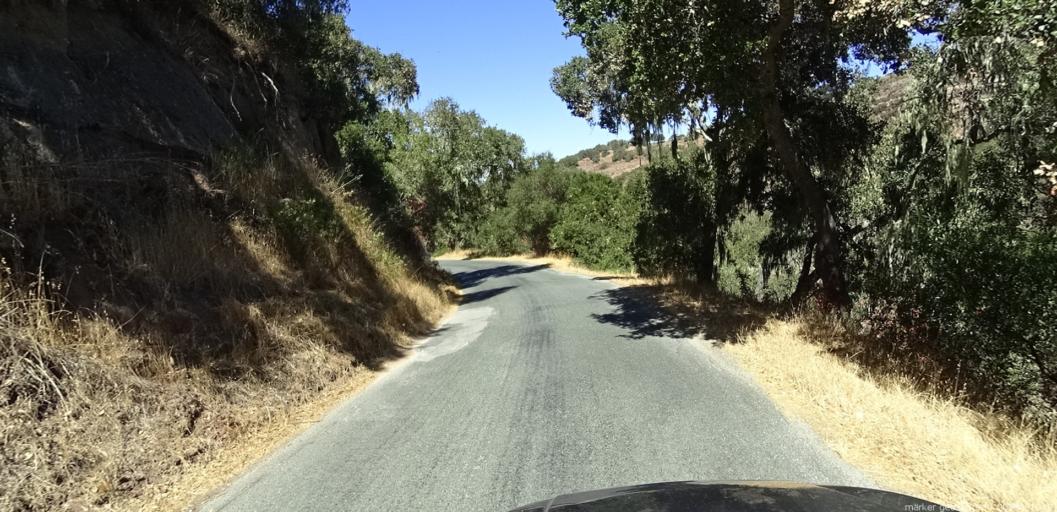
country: US
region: California
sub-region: Monterey County
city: Carmel Valley Village
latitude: 36.4855
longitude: -121.8063
